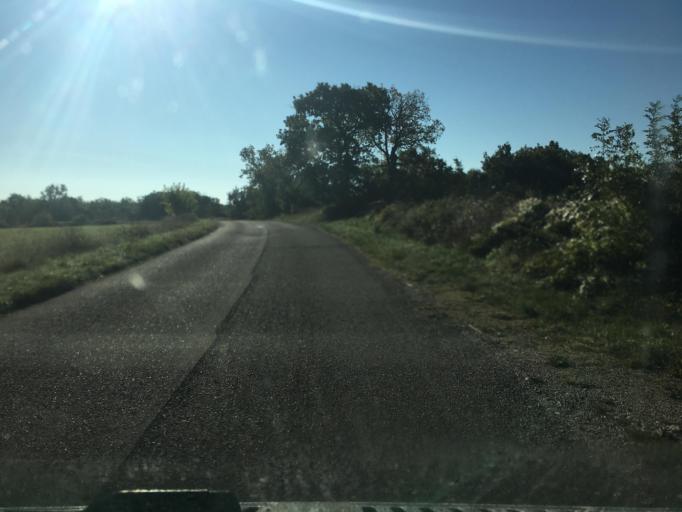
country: FR
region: Languedoc-Roussillon
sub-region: Departement du Gard
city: Barjac
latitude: 44.1789
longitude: 4.3368
